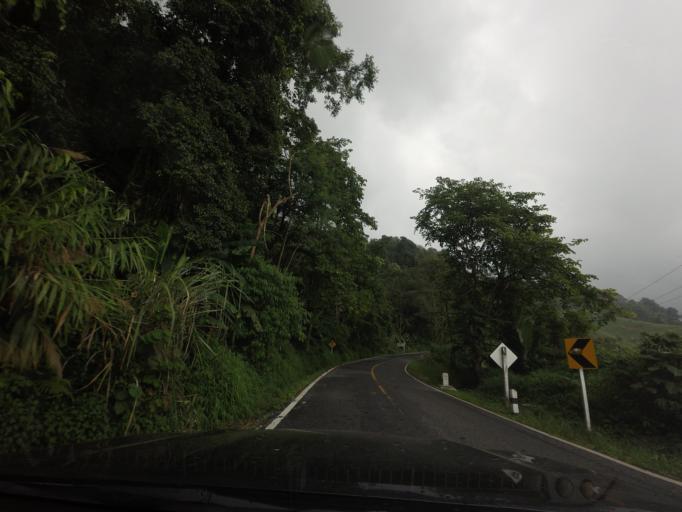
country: TH
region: Nan
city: Bo Kluea
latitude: 19.1822
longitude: 101.0789
